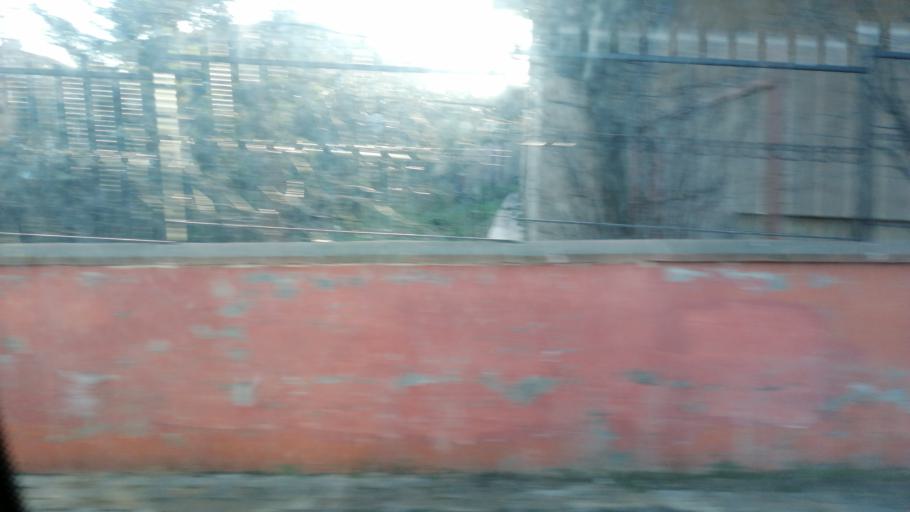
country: TR
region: Istanbul
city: UEskuedar
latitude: 41.0574
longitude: 29.0660
